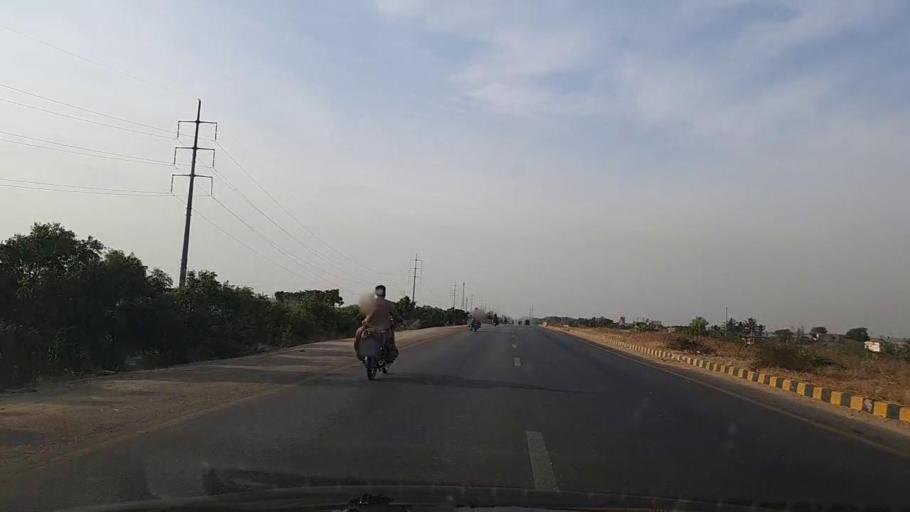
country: PK
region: Sindh
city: Gharo
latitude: 24.7753
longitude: 67.5421
